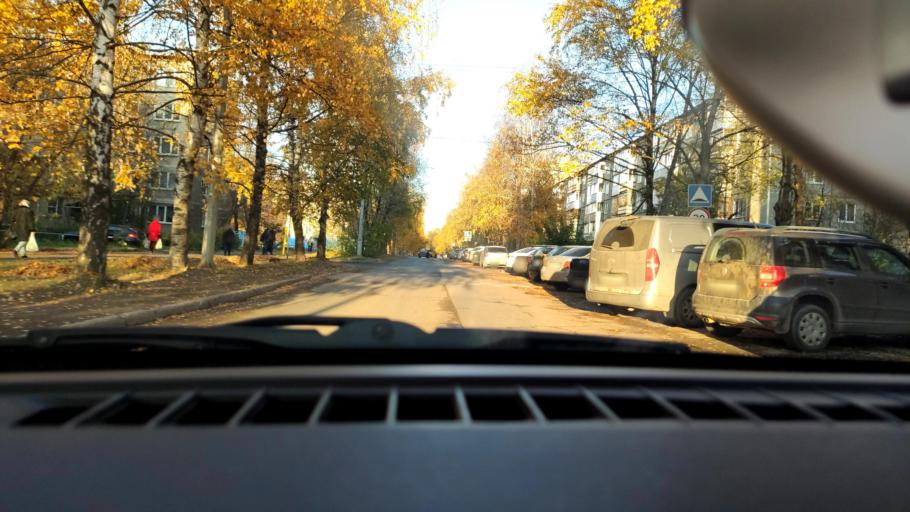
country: RU
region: Perm
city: Perm
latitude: 57.9653
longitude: 56.1855
